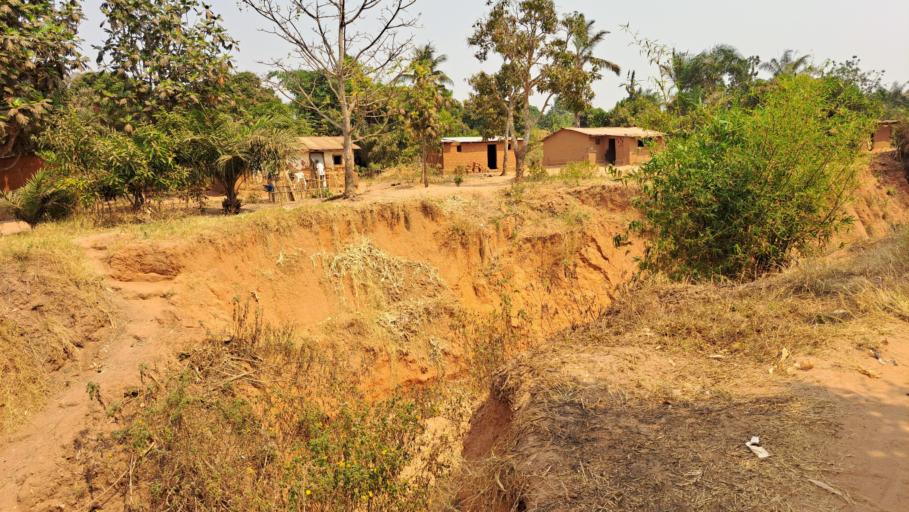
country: CD
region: Kasai-Oriental
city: Mbuji-Mayi
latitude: -6.0984
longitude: 23.5625
